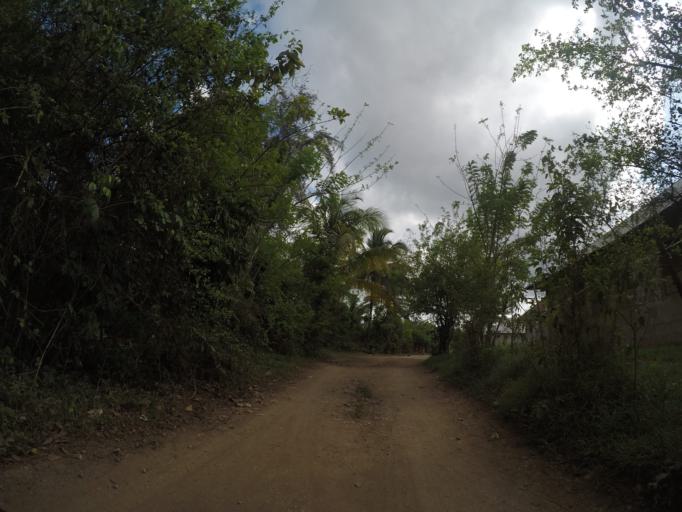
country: TZ
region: Zanzibar Central/South
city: Koani
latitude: -6.1981
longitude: 39.3161
